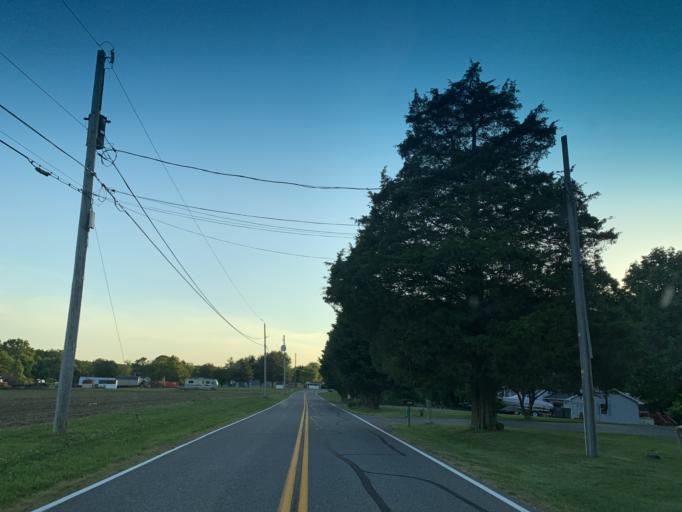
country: US
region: Maryland
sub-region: Cecil County
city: Perryville
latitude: 39.6280
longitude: -76.0638
